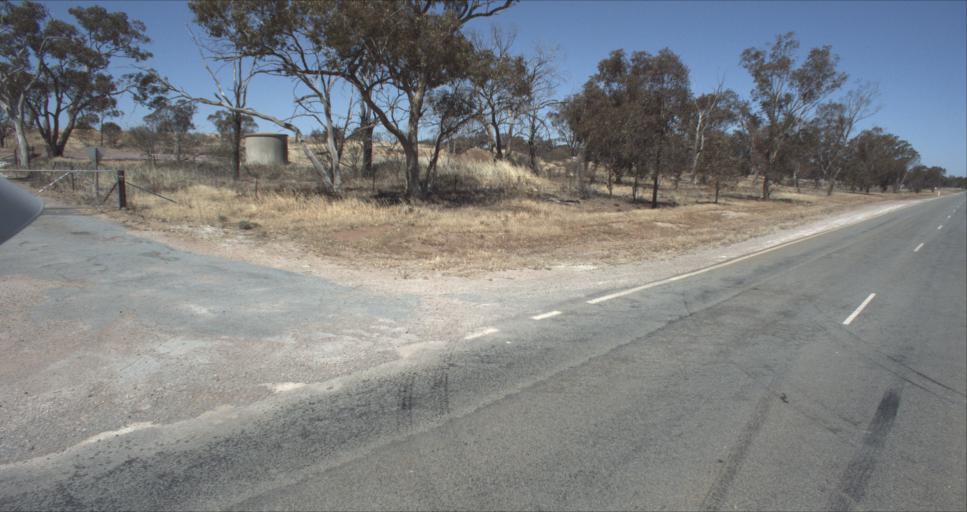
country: AU
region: New South Wales
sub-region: Leeton
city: Leeton
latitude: -34.4997
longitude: 146.4337
